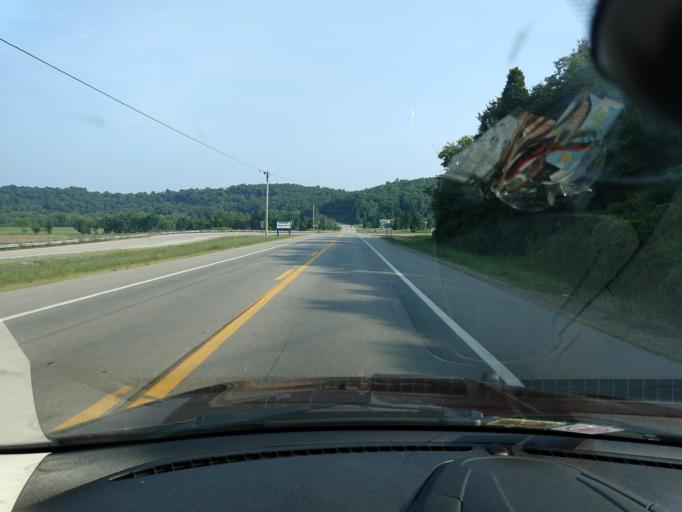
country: US
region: West Virginia
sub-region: Jackson County
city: Ripley
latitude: 38.8527
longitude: -81.8011
